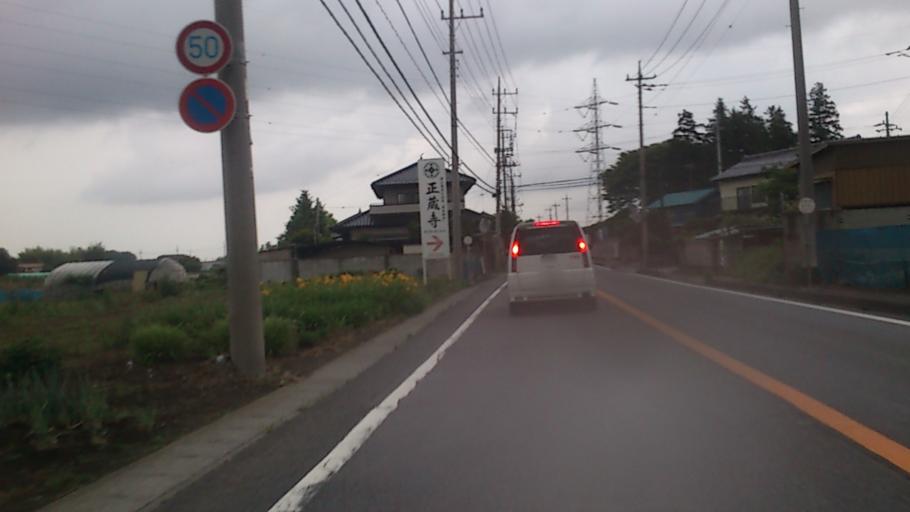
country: JP
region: Ibaraki
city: Koga
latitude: 36.1432
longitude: 139.7594
